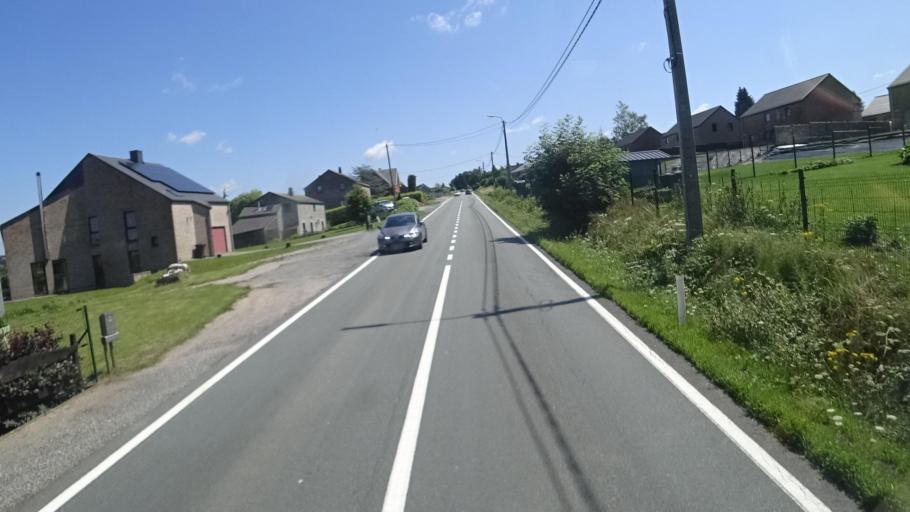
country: BE
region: Wallonia
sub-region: Province de Namur
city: Floreffe
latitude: 50.4179
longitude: 4.7797
